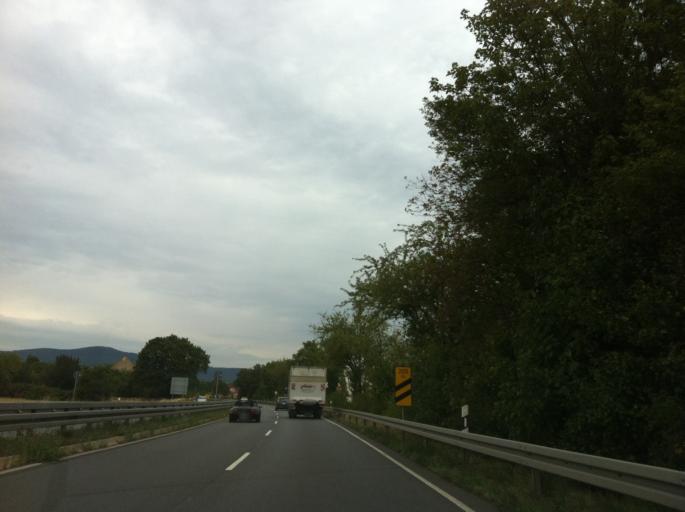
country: DE
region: Hesse
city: Schwalbach am Taunus
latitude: 50.1480
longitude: 8.5501
